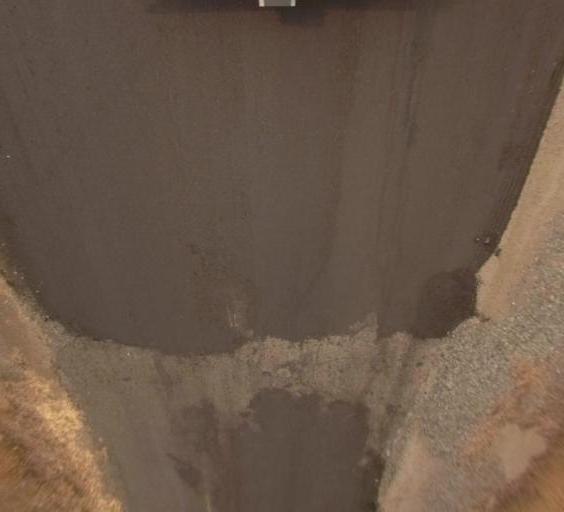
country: US
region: California
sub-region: Madera County
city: Coarsegold
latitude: 37.1773
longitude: -119.6824
